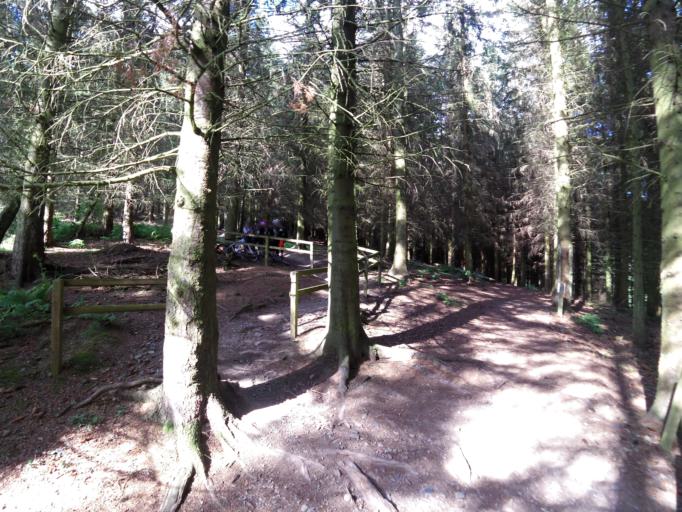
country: GB
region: Scotland
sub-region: The Scottish Borders
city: Peebles
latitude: 55.6494
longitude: -3.1360
